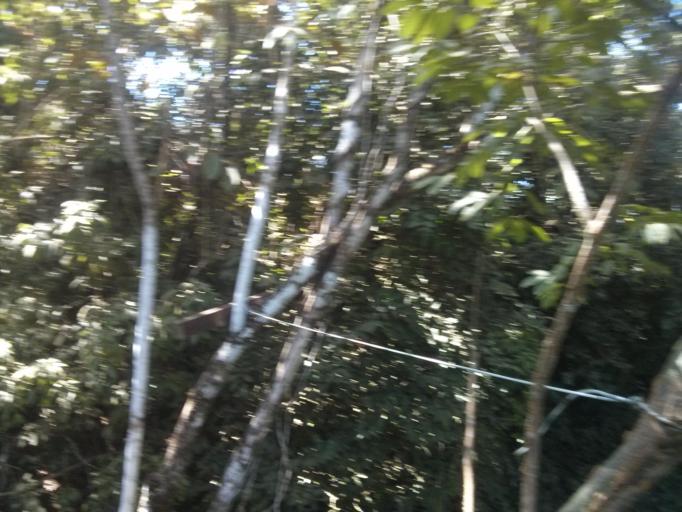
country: CR
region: Puntarenas
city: Paquera
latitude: 9.6541
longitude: -85.0776
